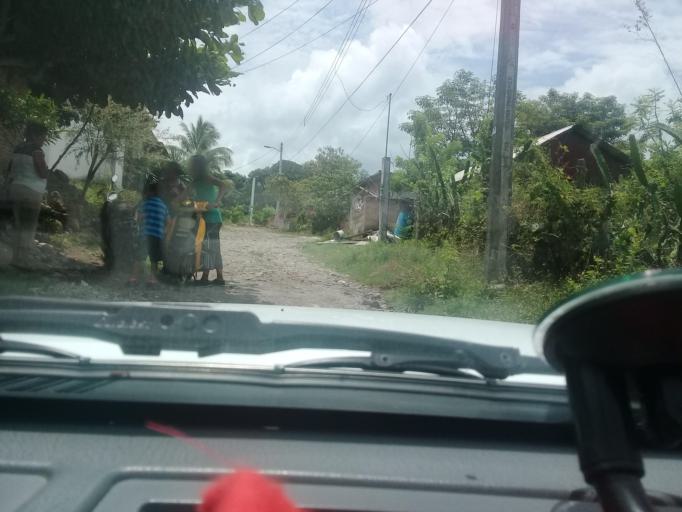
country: MX
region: Veracruz
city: Paso de Ovejas
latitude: 19.2785
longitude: -96.4318
